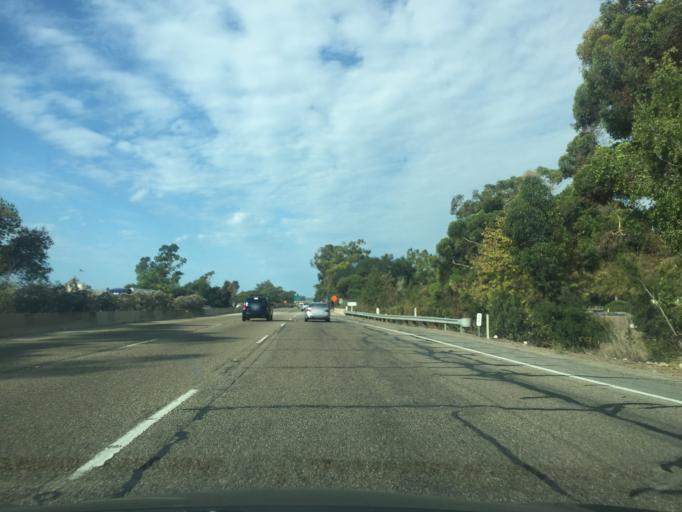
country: US
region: California
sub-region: Santa Barbara County
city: Goleta
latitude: 34.4412
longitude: -119.8154
